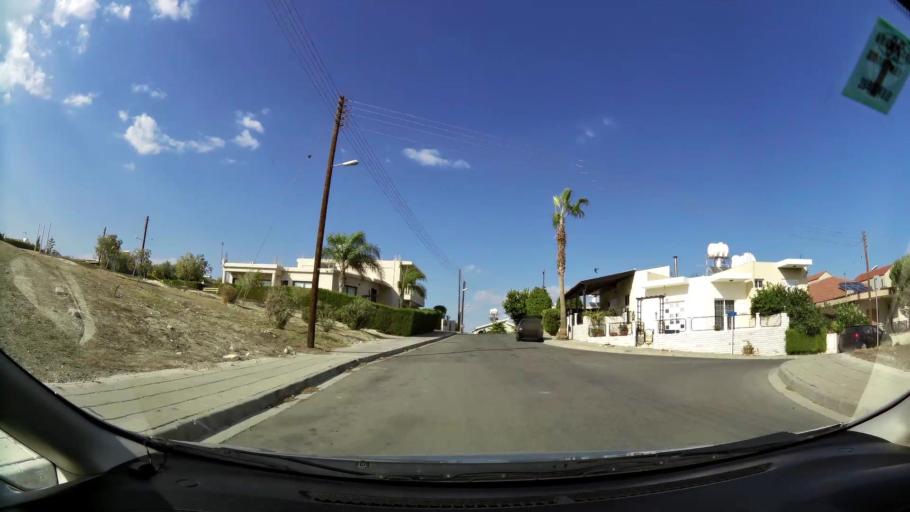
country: CY
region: Larnaka
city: Livadia
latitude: 34.9456
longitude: 33.6219
